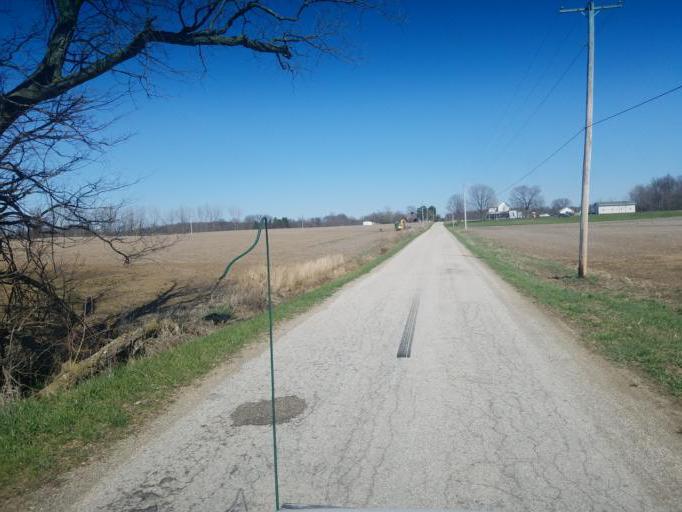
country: US
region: Ohio
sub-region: Morrow County
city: Mount Gilead
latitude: 40.5865
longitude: -82.8874
